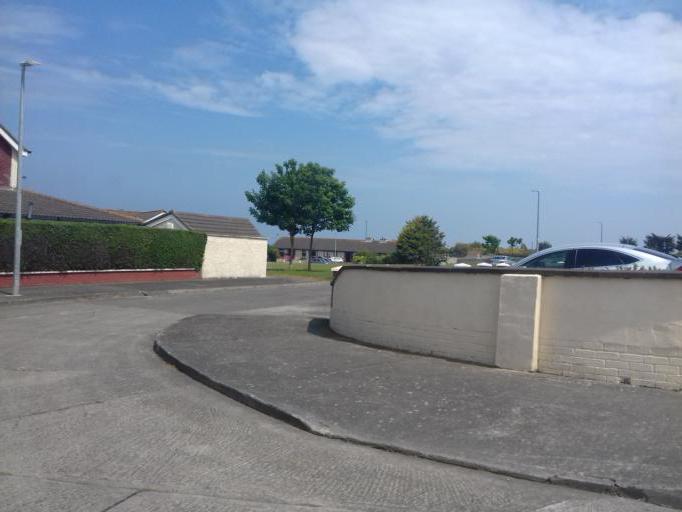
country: IE
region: Leinster
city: Portraine
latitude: 53.4916
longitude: -6.1056
